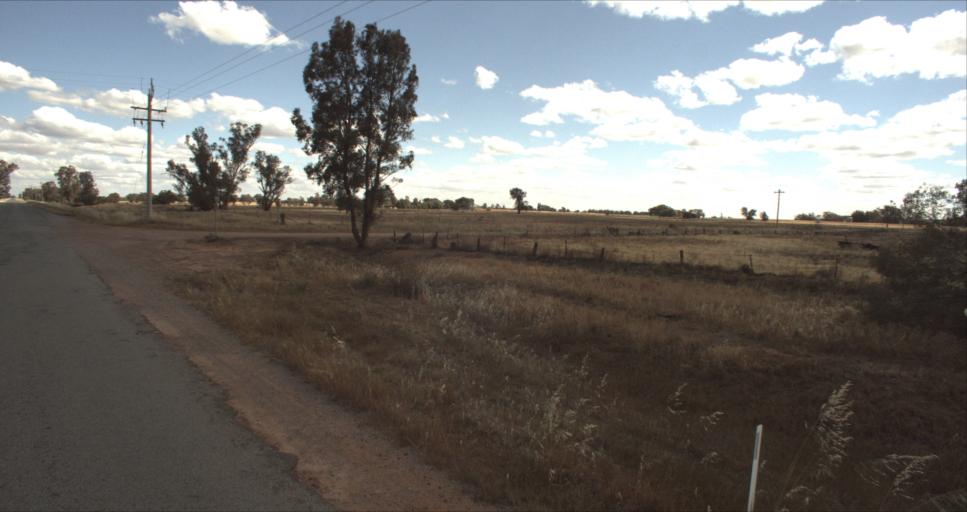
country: AU
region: New South Wales
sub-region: Leeton
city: Leeton
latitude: -34.4821
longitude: 146.2489
